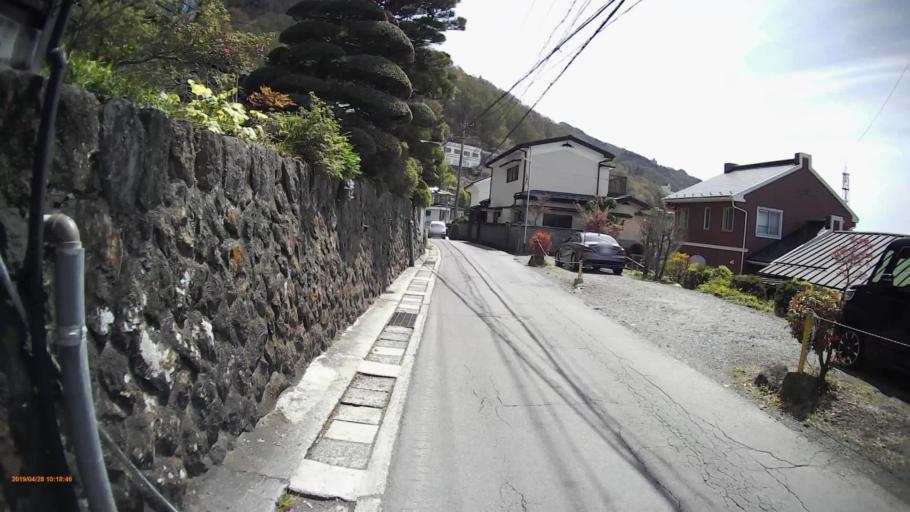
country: JP
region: Nagano
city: Suwa
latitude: 36.0638
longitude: 138.1100
